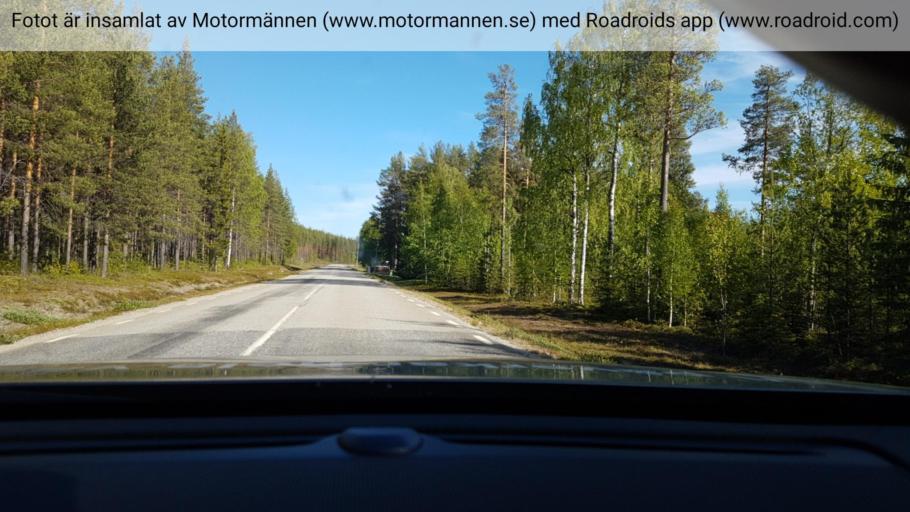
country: SE
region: Vaesterbotten
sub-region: Lycksele Kommun
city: Lycksele
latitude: 64.7858
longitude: 18.9860
